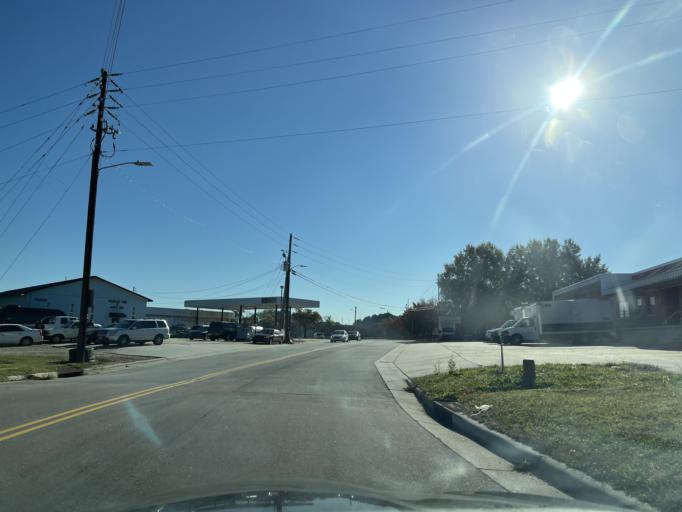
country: US
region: North Carolina
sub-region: Wake County
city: Raleigh
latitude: 35.8131
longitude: -78.6152
